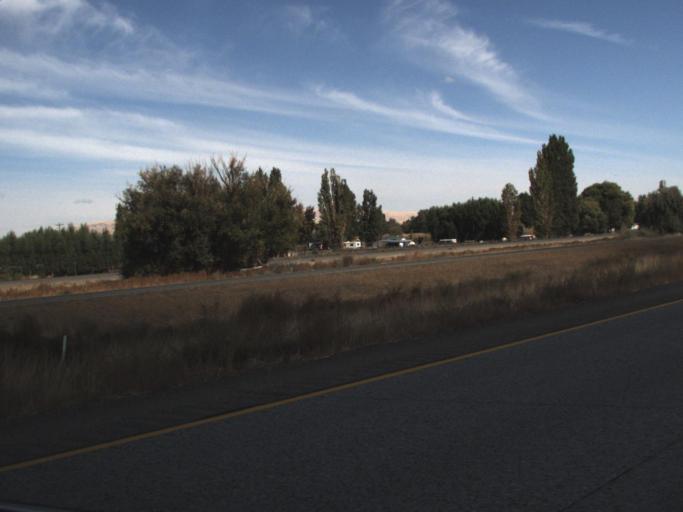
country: US
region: Washington
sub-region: Yakima County
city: Granger
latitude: 46.3296
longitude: -120.1021
